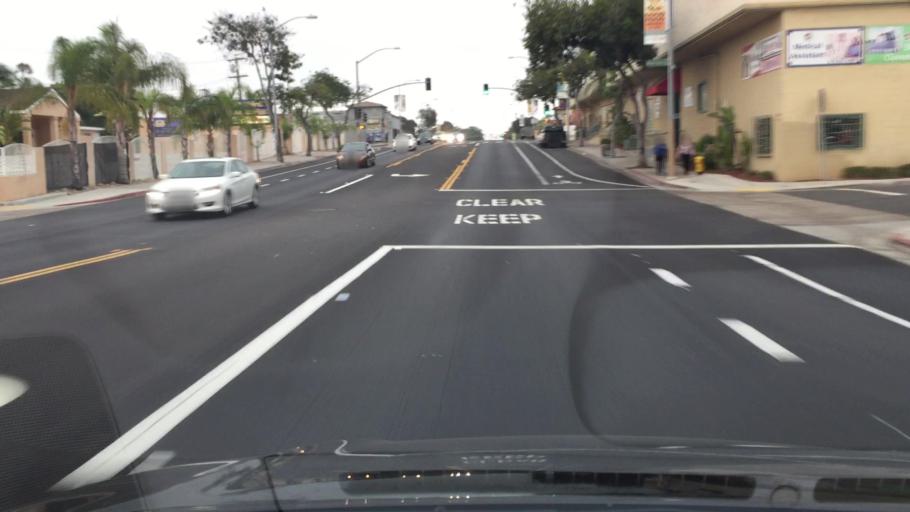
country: US
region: California
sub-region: San Diego County
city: National City
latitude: 32.7115
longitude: -117.1058
